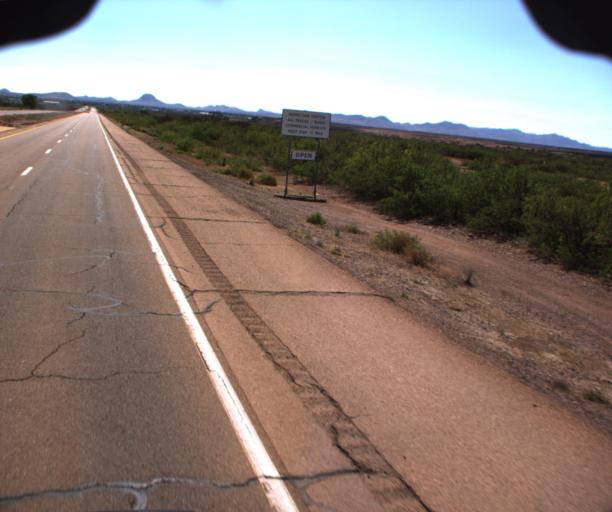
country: US
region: Arizona
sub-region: Cochise County
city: Pirtleville
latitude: 31.3540
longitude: -109.5963
